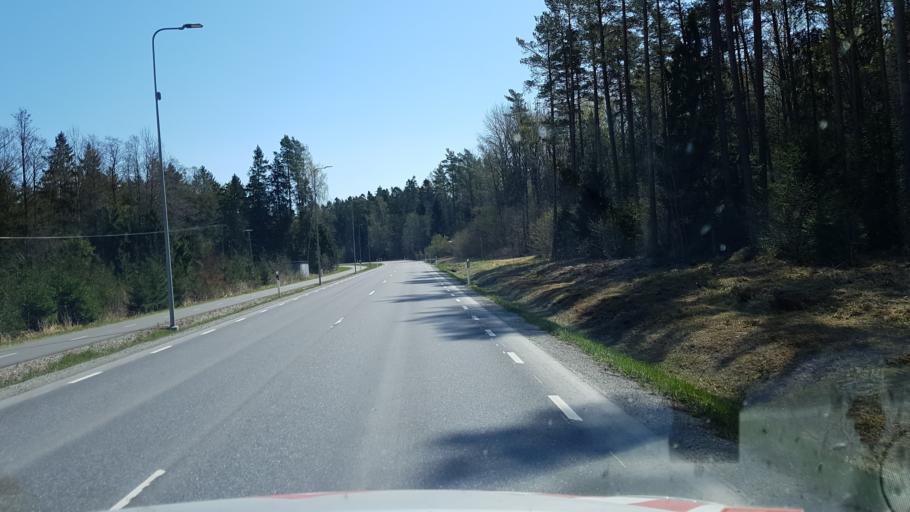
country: EE
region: Harju
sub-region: Viimsi vald
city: Viimsi
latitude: 59.5251
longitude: 24.8843
